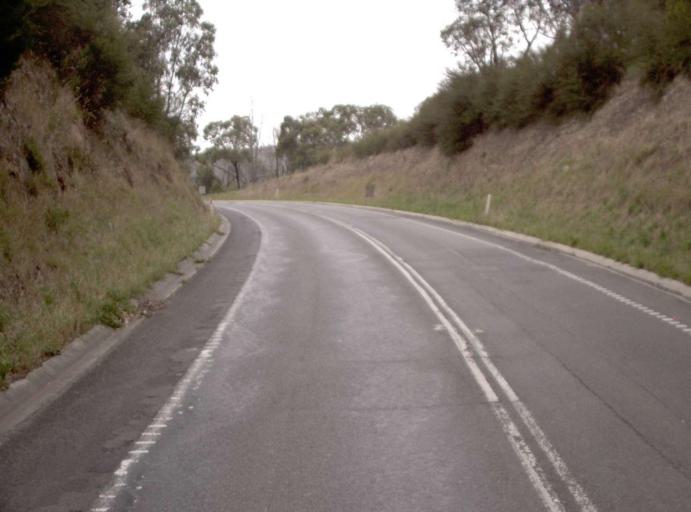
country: AU
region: Victoria
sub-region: Yarra Ranges
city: Yarra Glen
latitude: -37.5669
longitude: 145.4161
